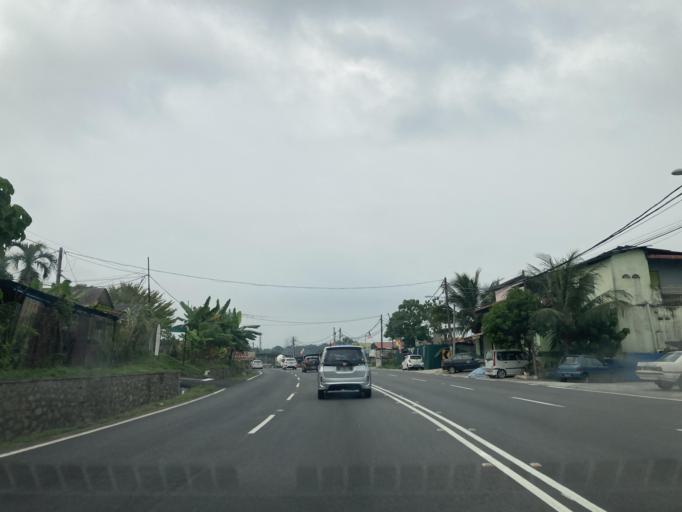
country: MY
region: Selangor
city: Kuang
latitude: 3.2123
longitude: 101.5350
